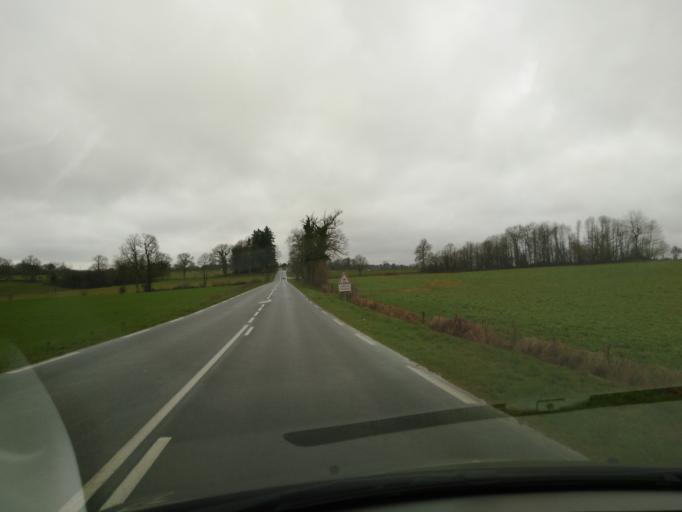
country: FR
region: Limousin
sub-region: Departement de la Haute-Vienne
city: Nexon
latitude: 45.6895
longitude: 1.2297
